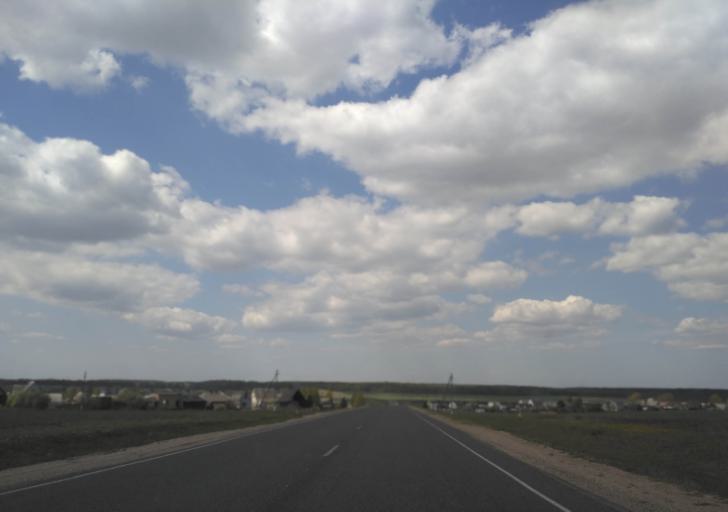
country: BY
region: Minsk
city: Vilyeyka
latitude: 54.5161
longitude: 26.9835
